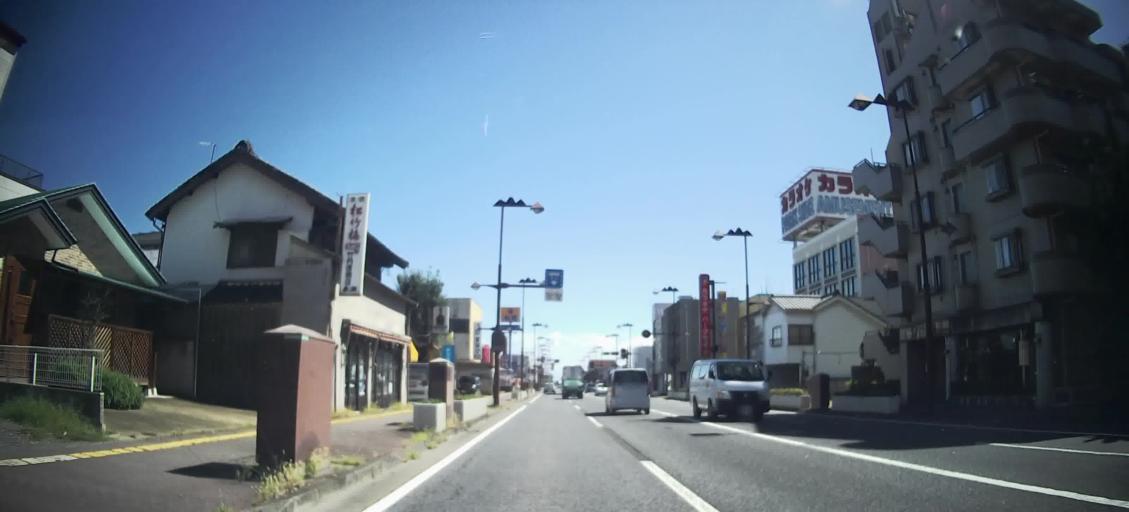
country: JP
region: Gunma
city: Maebashi-shi
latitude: 36.3854
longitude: 139.0794
